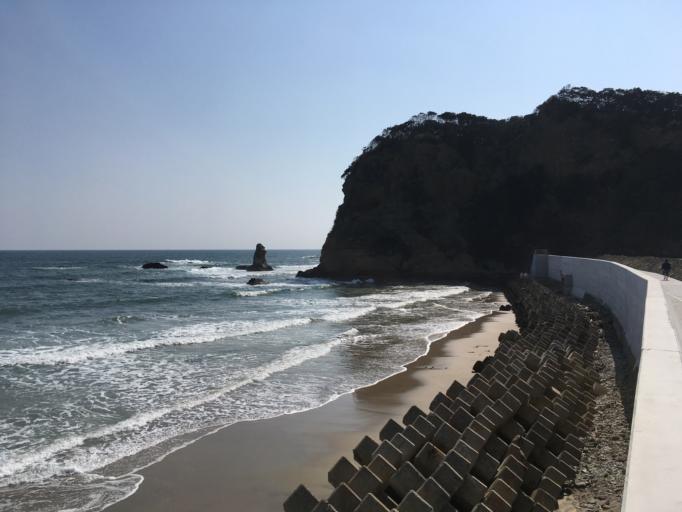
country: JP
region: Fukushima
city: Iwaki
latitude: 36.9749
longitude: 140.9672
